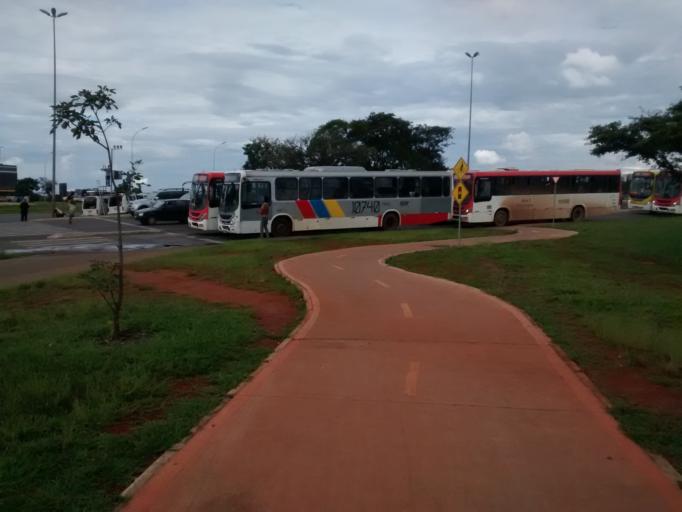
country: BR
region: Federal District
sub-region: Brasilia
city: Brasilia
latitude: -15.7938
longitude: -47.8810
